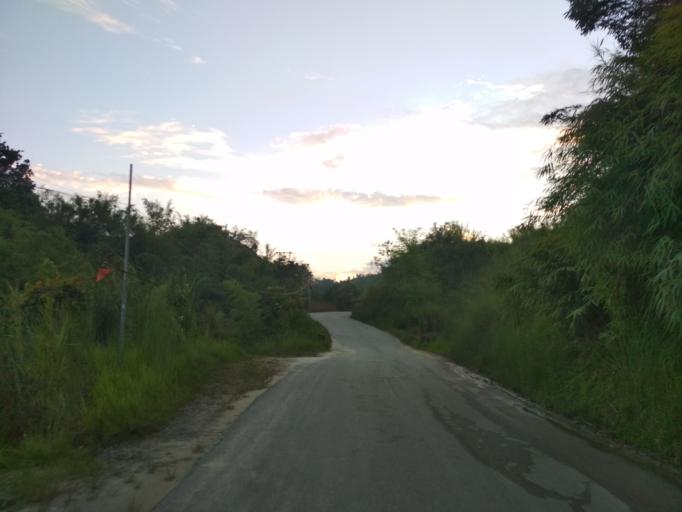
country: IN
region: Arunachal Pradesh
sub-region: Papum Pare
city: Naharlagun
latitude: 27.0936
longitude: 93.6654
